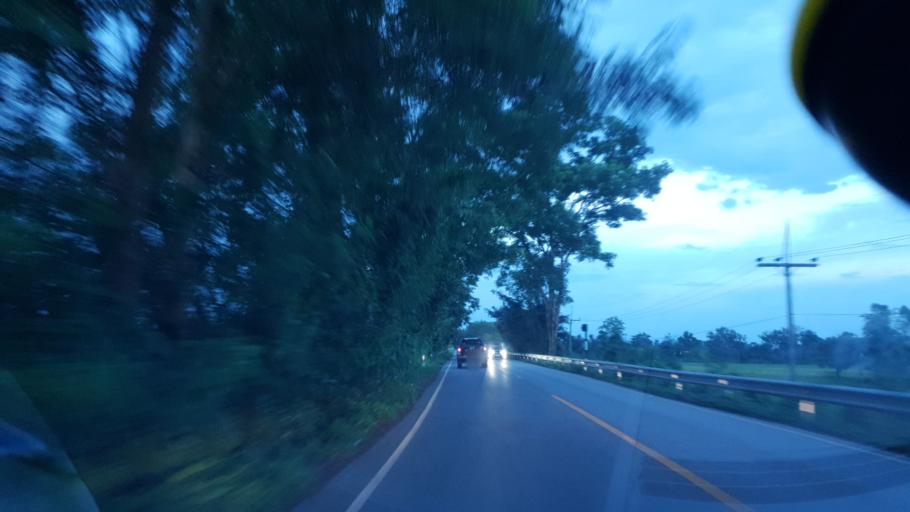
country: TH
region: Chiang Rai
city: Wiang Chiang Rung
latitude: 19.9719
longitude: 99.9734
